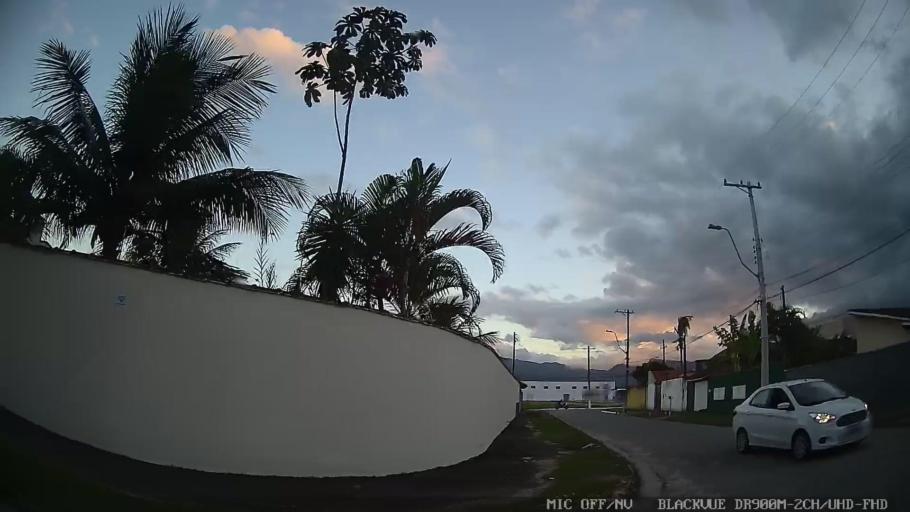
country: BR
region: Sao Paulo
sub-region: Caraguatatuba
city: Caraguatatuba
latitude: -23.6661
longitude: -45.4480
